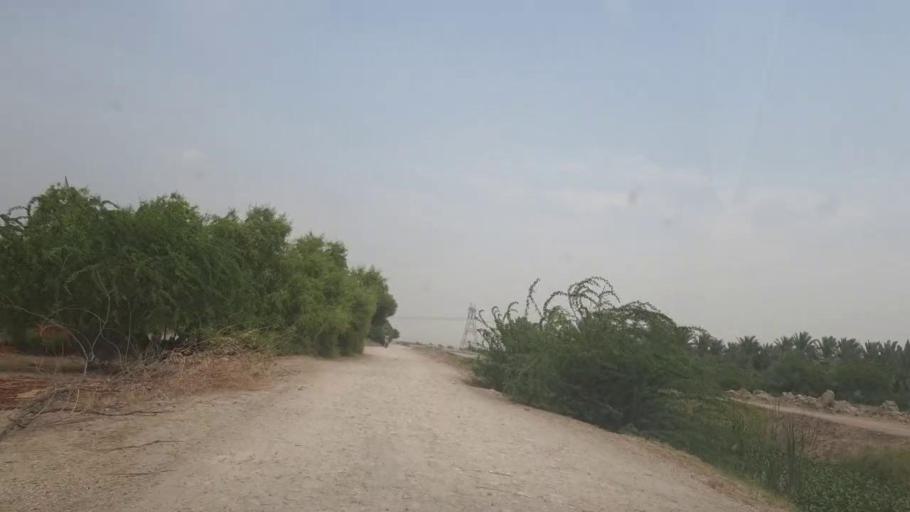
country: PK
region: Sindh
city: Kot Diji
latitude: 27.4252
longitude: 68.6811
